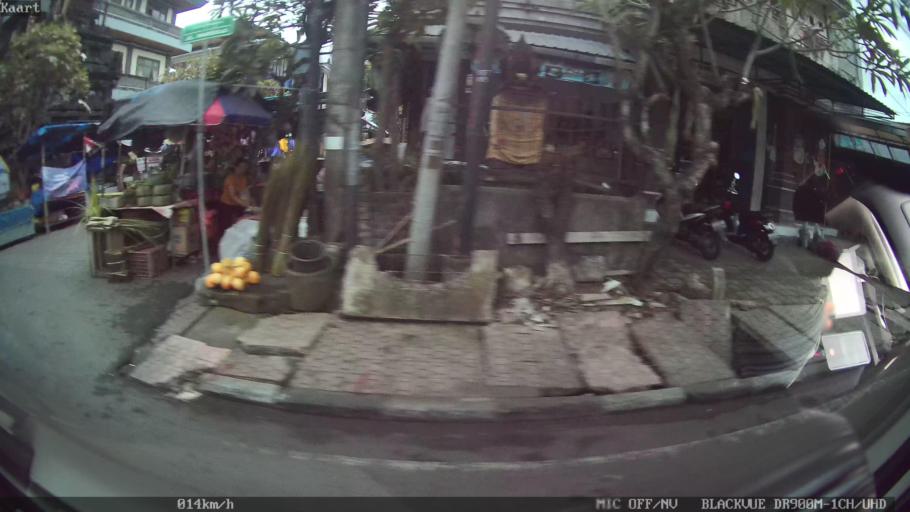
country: ID
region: Bali
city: Banjar Bucu
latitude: -8.5871
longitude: 115.2064
